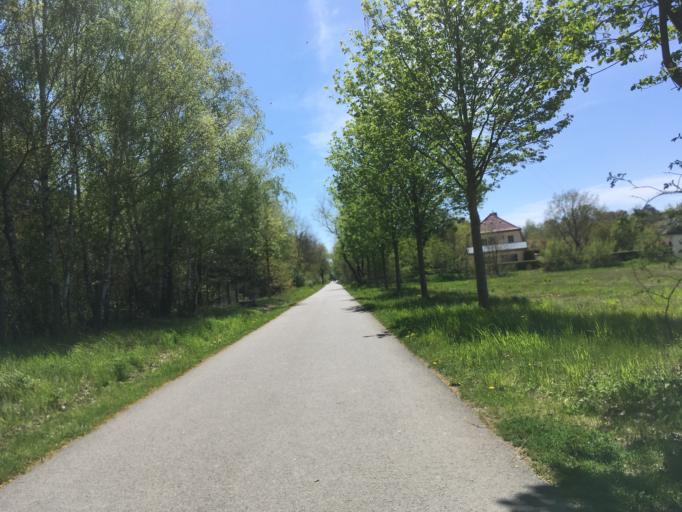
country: DE
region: Brandenburg
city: Konigs Wusterhausen
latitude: 52.3086
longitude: 13.6168
